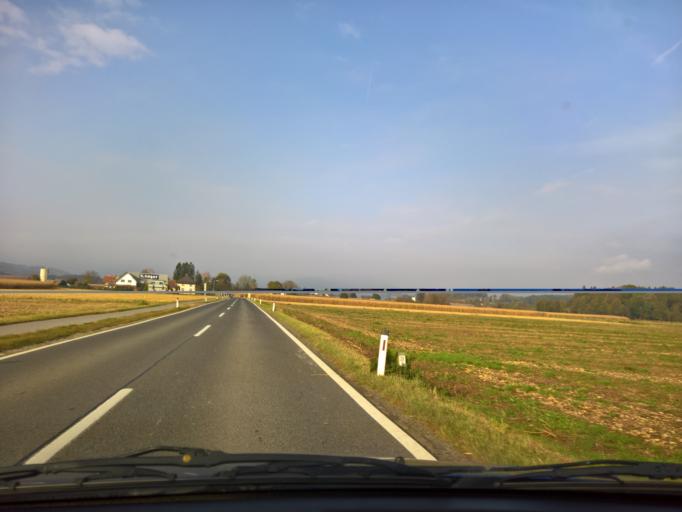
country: AT
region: Styria
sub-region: Politischer Bezirk Deutschlandsberg
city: Gross Sankt Florian
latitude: 46.8229
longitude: 15.2931
